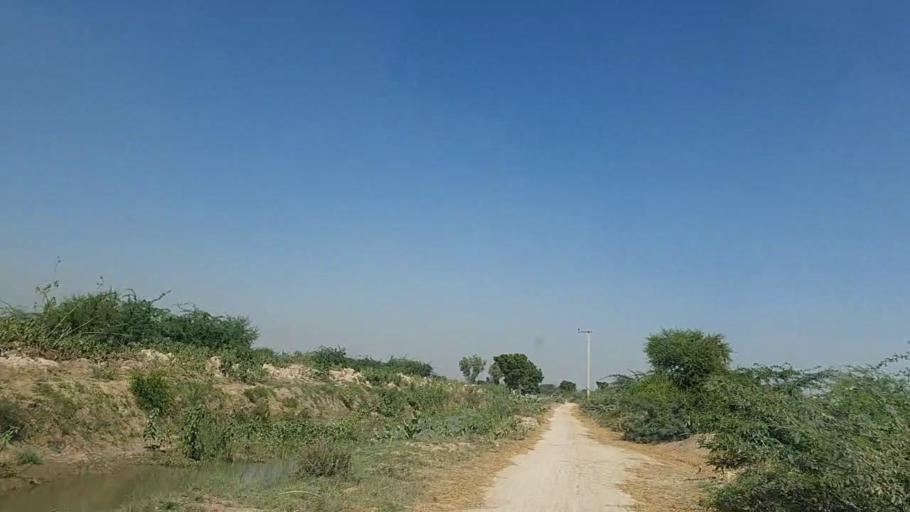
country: PK
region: Sindh
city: Daro Mehar
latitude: 24.7682
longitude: 68.1554
